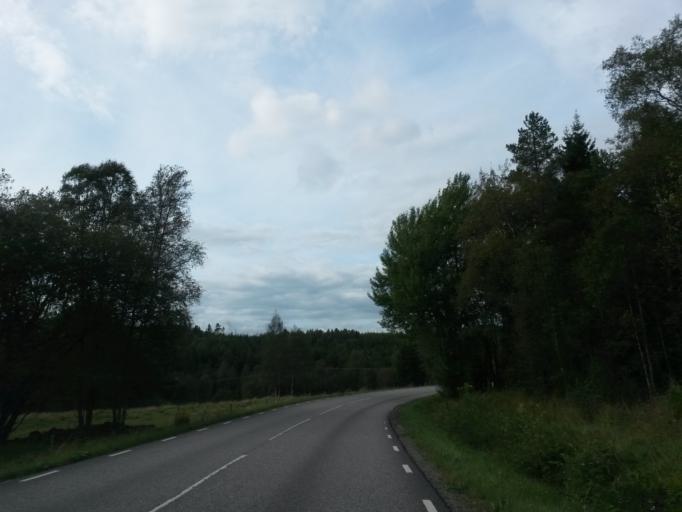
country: SE
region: Vaestra Goetaland
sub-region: Boras Kommun
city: Ganghester
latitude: 57.7754
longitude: 13.0224
